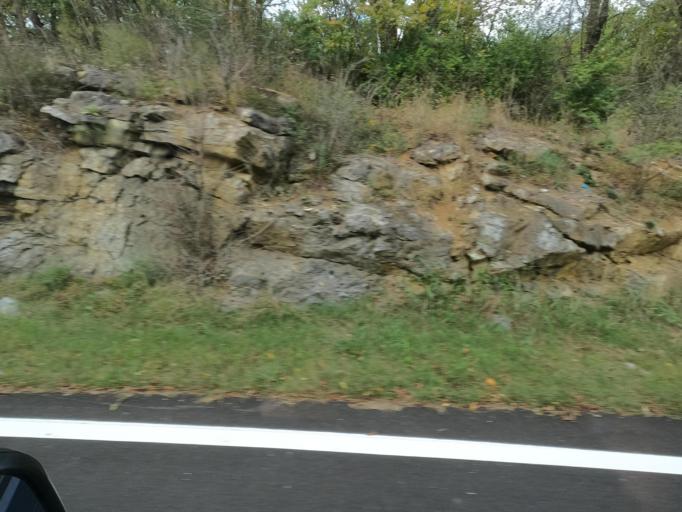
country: US
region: Tennessee
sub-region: Carter County
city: Pine Crest
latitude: 36.3262
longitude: -82.3238
